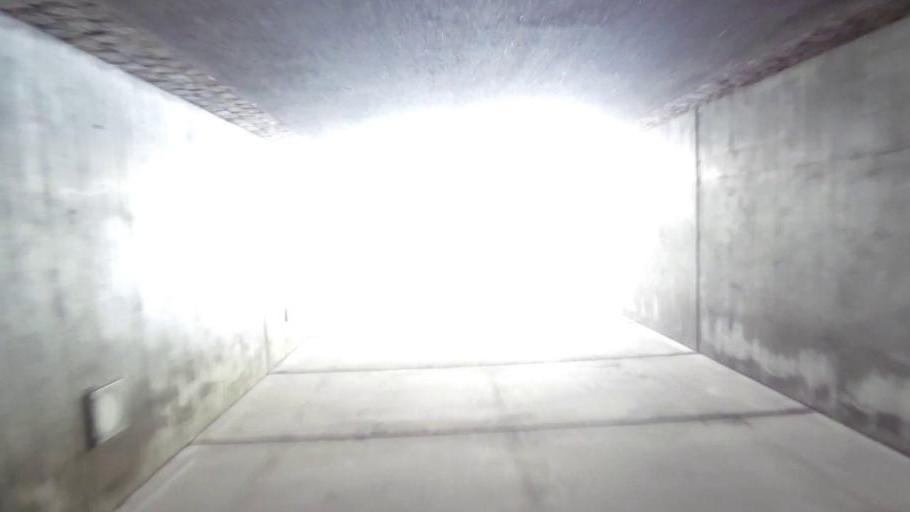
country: SE
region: OEstergoetland
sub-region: Linkopings Kommun
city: Malmslatt
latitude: 58.3999
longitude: 15.5519
